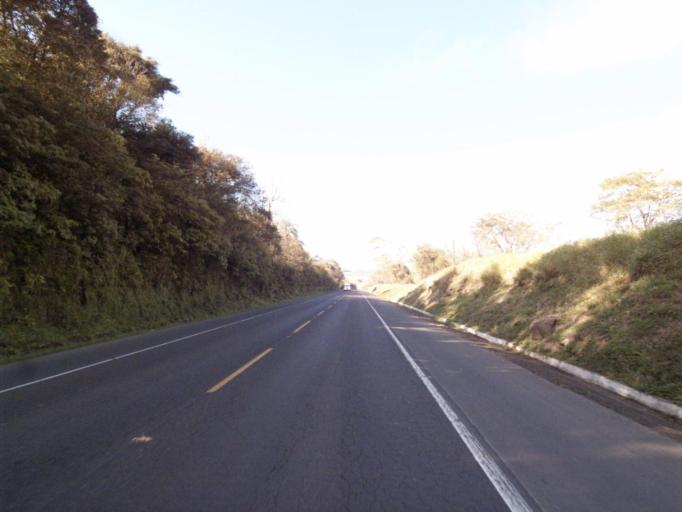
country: BR
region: Rio Grande do Sul
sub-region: Frederico Westphalen
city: Frederico Westphalen
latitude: -27.0393
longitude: -53.2284
